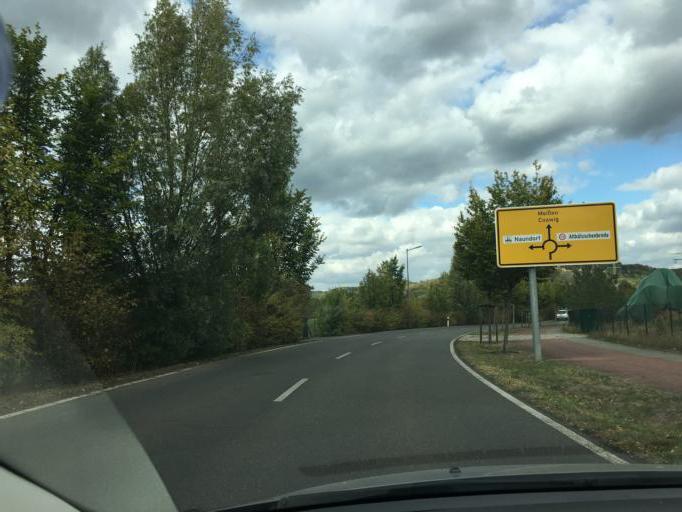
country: DE
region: Saxony
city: Coswig
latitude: 51.1079
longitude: 13.6099
